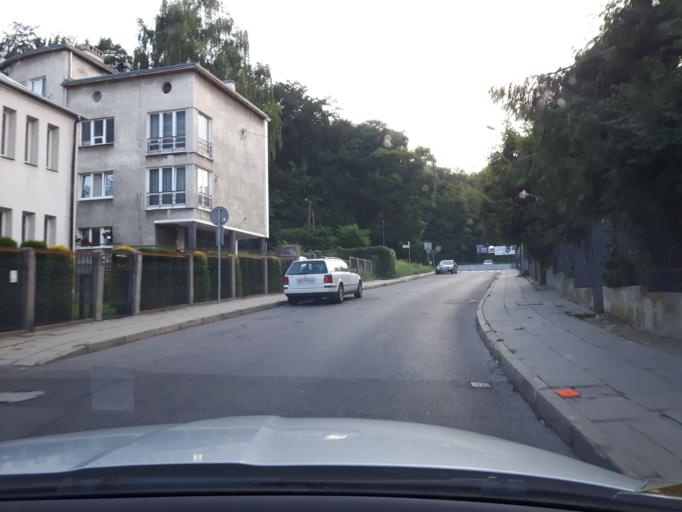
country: PL
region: Pomeranian Voivodeship
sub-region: Gdynia
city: Gdynia
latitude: 54.5141
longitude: 18.5252
